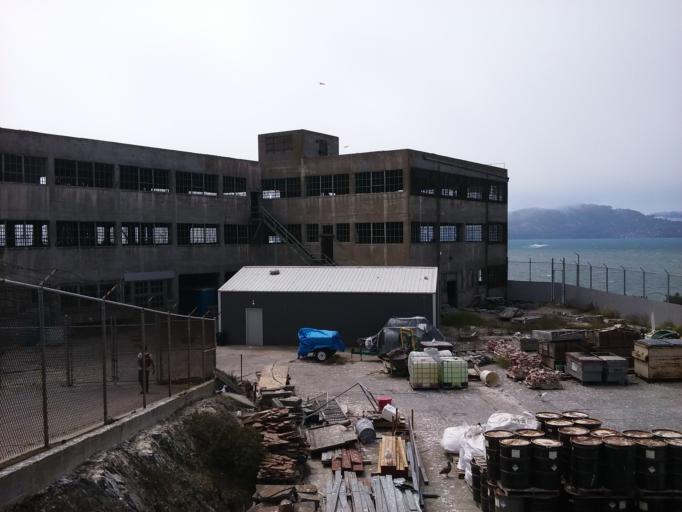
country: US
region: California
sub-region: San Francisco County
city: San Francisco
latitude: 37.8281
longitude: -122.4247
